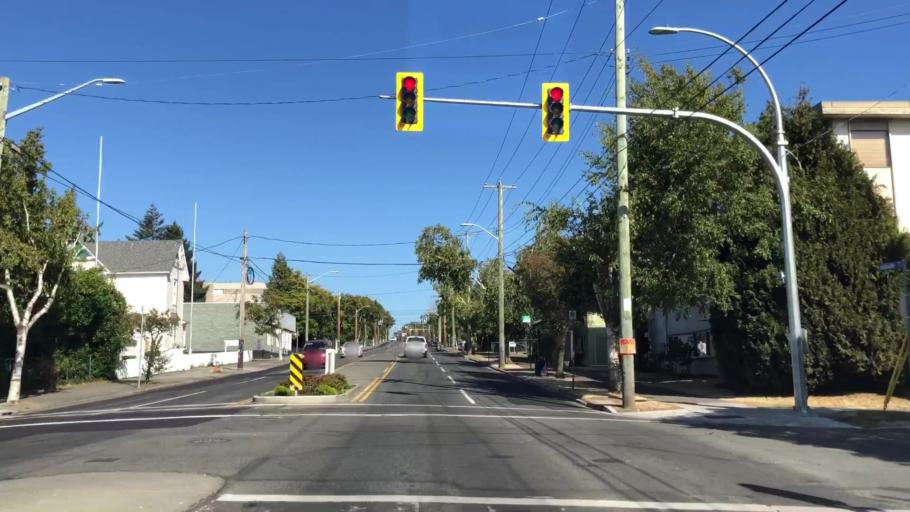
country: CA
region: British Columbia
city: Victoria
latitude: 48.4398
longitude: -123.3566
